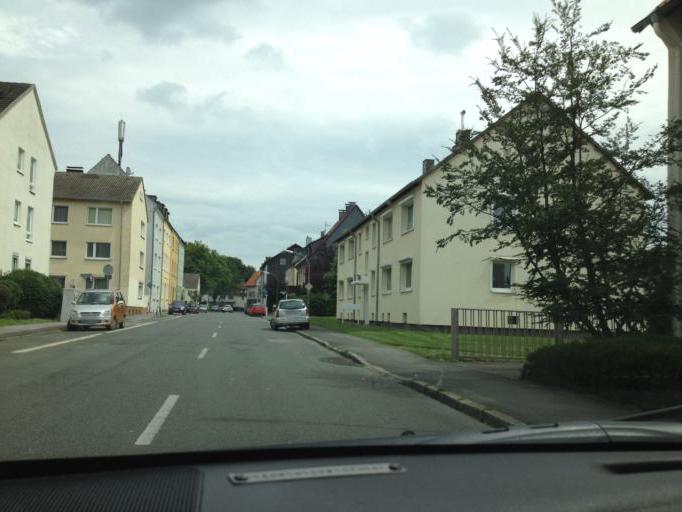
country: DE
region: North Rhine-Westphalia
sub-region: Regierungsbezirk Arnsberg
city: Dortmund
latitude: 51.4700
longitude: 7.4400
